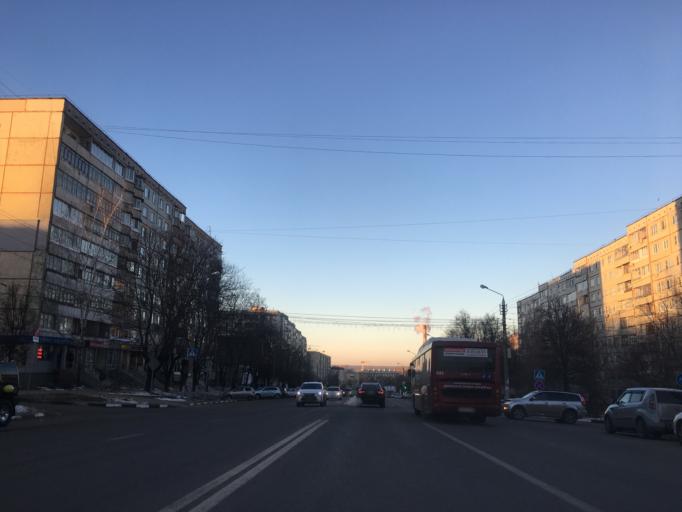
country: RU
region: Tula
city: Tula
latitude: 54.1926
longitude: 37.5914
